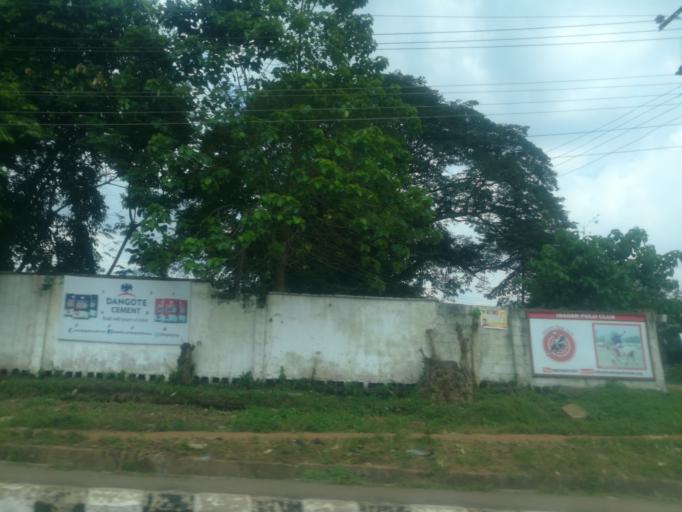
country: NG
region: Oyo
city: Ibadan
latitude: 7.4035
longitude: 3.8711
